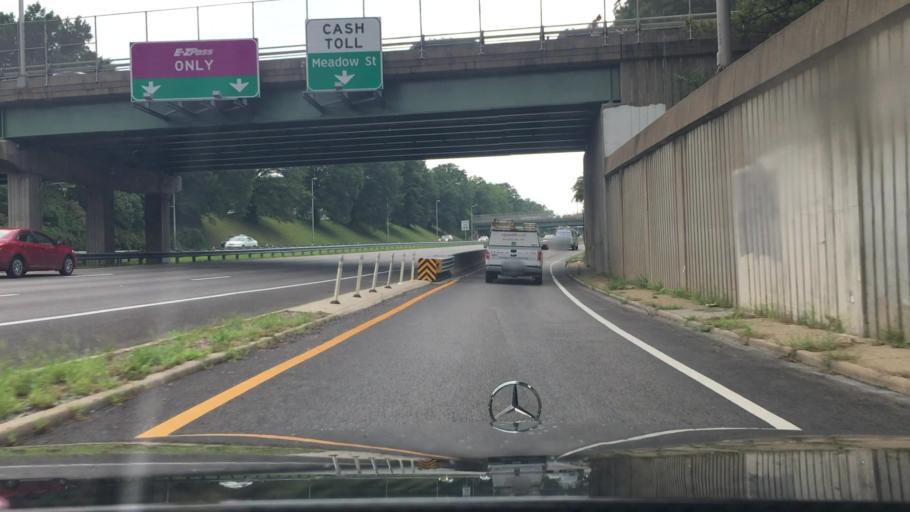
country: US
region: Virginia
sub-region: City of Richmond
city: Richmond
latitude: 37.5433
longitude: -77.4561
